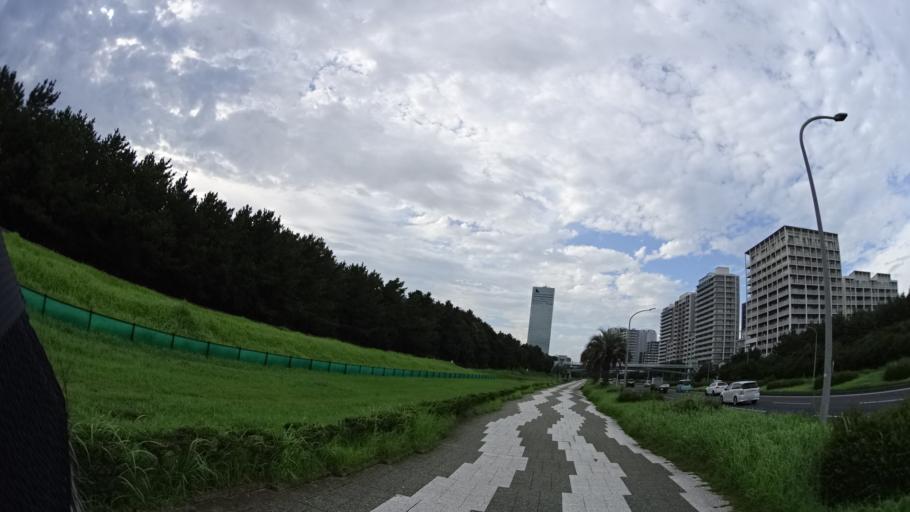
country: JP
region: Chiba
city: Funabashi
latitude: 35.6368
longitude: 140.0399
